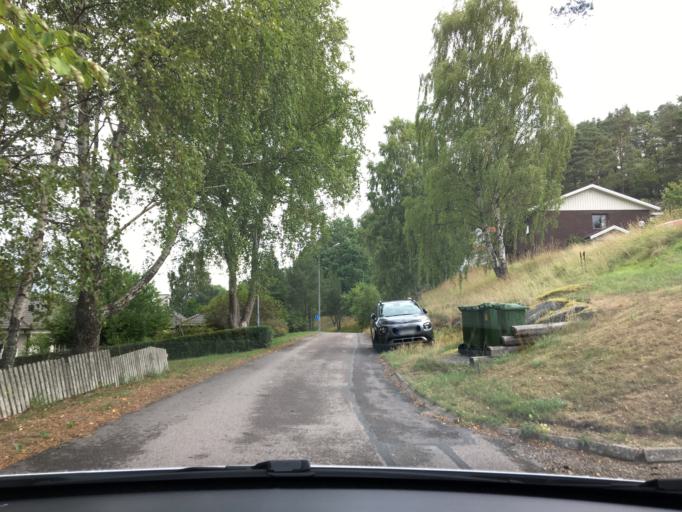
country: SE
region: Vaestra Goetaland
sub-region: Ale Kommun
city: Nodinge-Nol
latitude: 57.8934
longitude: 12.0620
